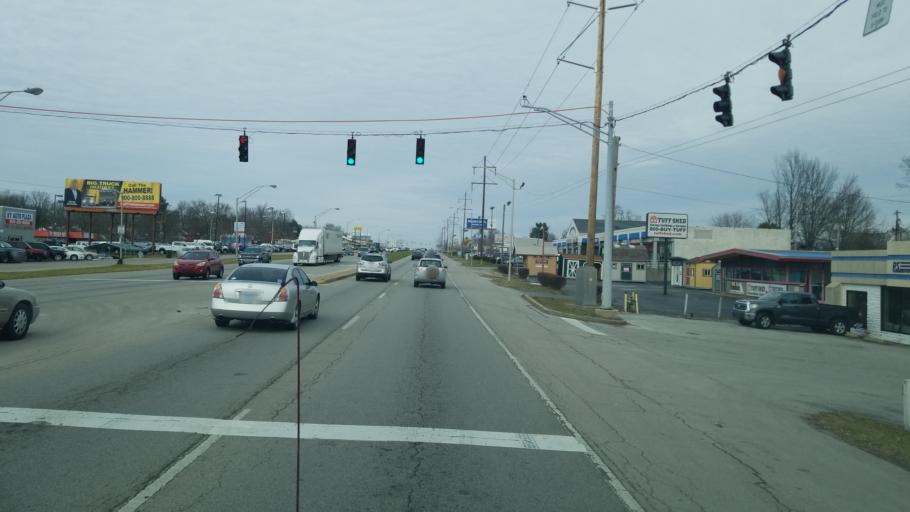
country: US
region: Kentucky
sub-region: Fayette County
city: Lexington-Fayette
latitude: 38.0516
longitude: -84.4567
